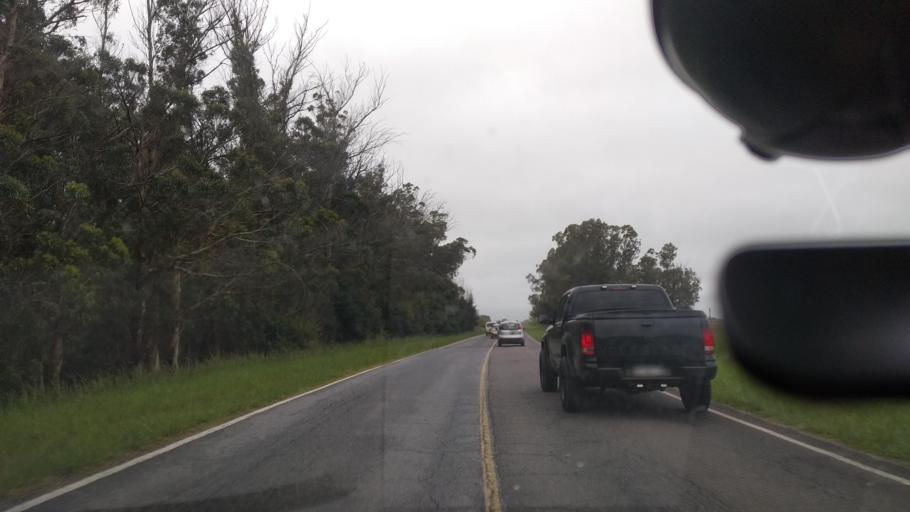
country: AR
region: Buenos Aires
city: Veronica
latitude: -35.5100
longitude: -57.3361
